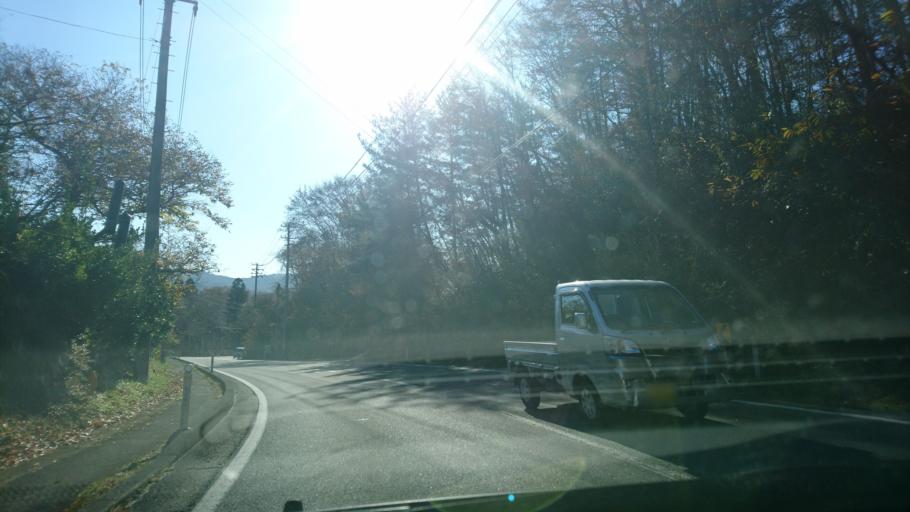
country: JP
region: Iwate
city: Ichinoseki
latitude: 38.9937
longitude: 141.2793
